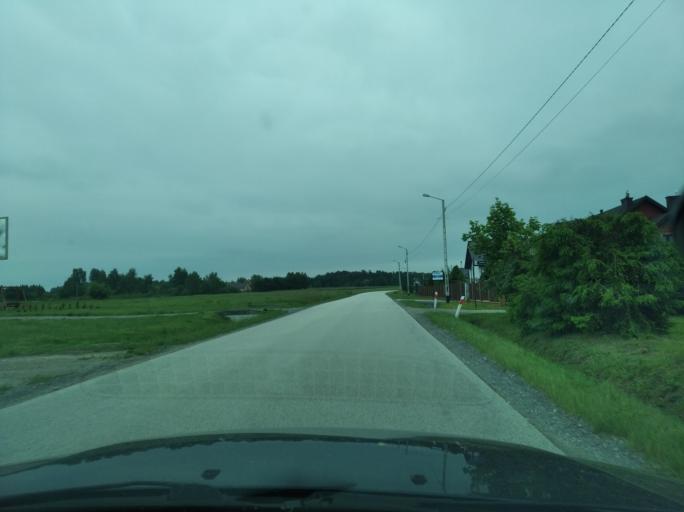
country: PL
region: Subcarpathian Voivodeship
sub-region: Powiat ropczycko-sedziszowski
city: Sedziszow Malopolski
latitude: 50.1221
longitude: 21.6733
